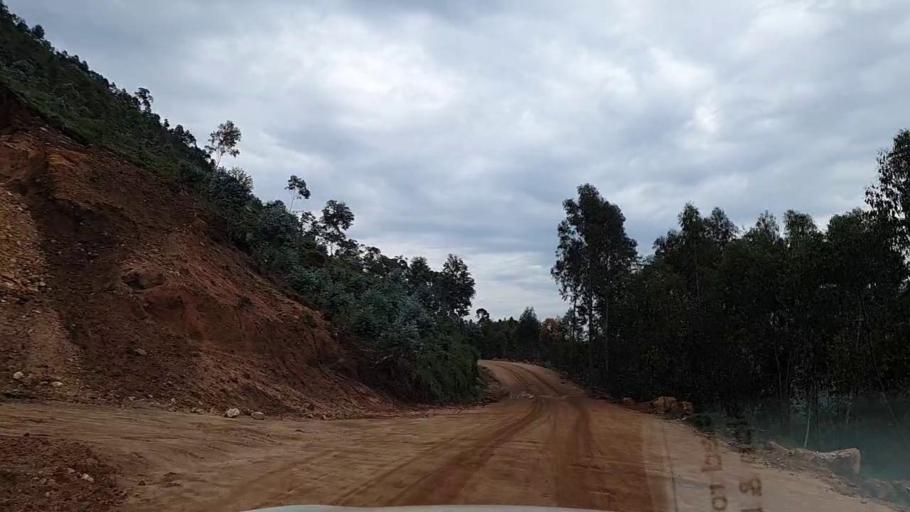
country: RW
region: Southern Province
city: Nzega
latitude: -2.3742
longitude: 29.4489
